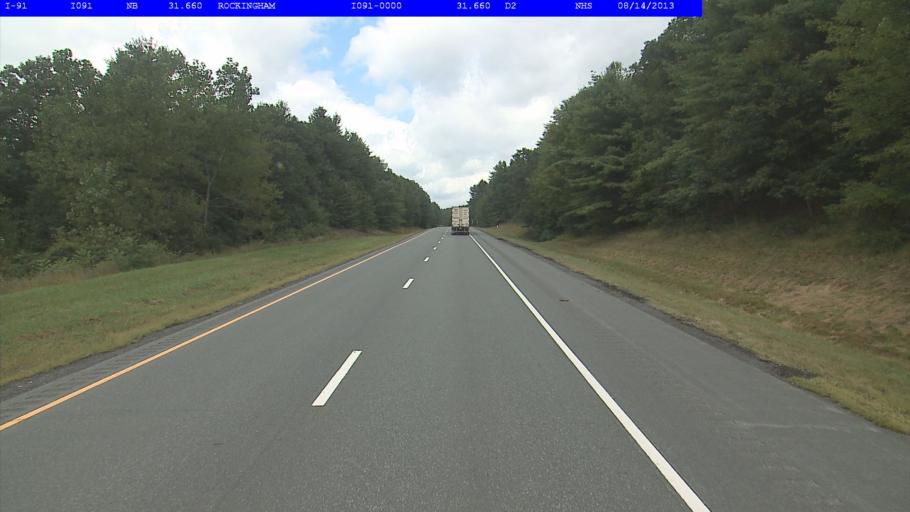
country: US
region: Vermont
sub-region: Windham County
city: Bellows Falls
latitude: 43.1307
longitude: -72.4736
